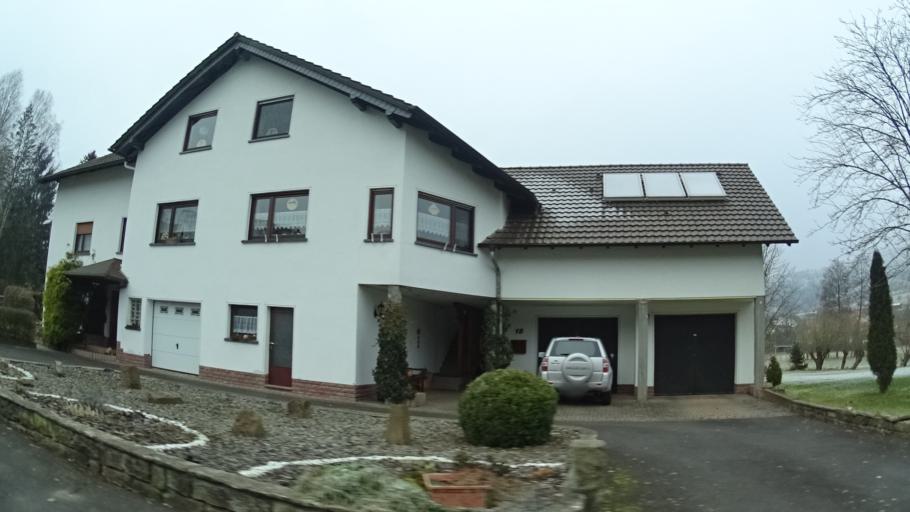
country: DE
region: Hesse
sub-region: Regierungsbezirk Darmstadt
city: Steinau an der Strasse
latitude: 50.2561
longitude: 9.5134
